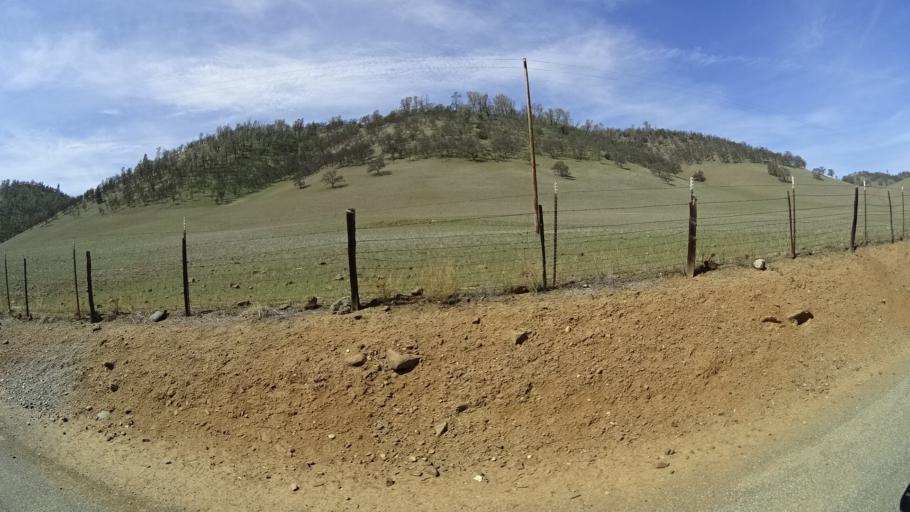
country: US
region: California
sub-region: Glenn County
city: Willows
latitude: 39.5103
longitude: -122.4543
